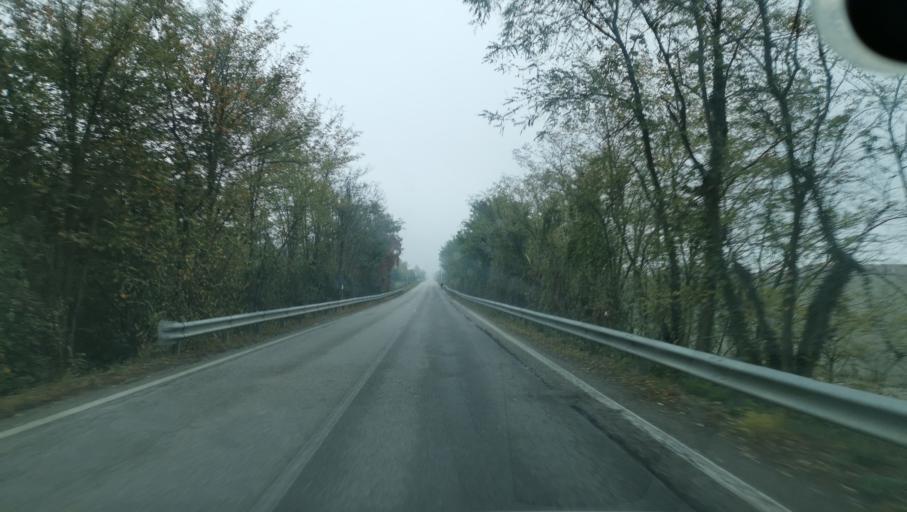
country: IT
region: Piedmont
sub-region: Provincia di Vercelli
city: Alice Castello
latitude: 45.3852
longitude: 8.0851
